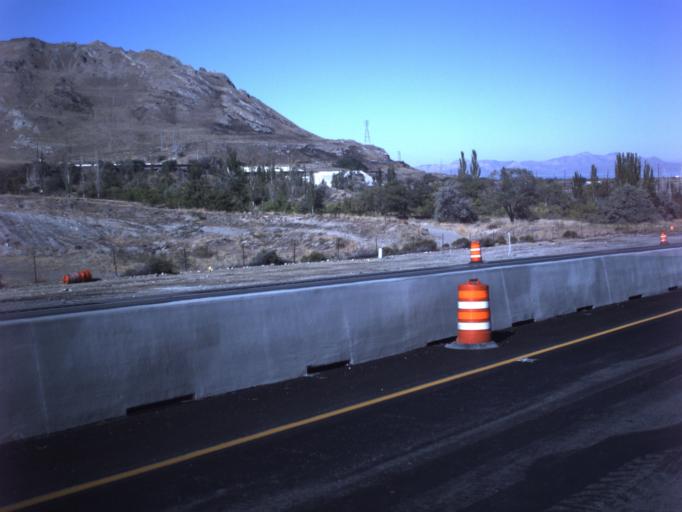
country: US
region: Utah
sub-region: Salt Lake County
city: Magna
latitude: 40.7243
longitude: -112.1598
